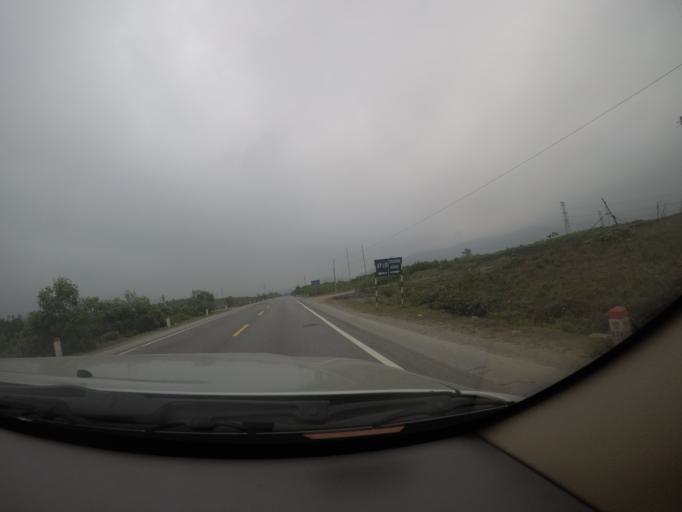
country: VN
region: Ha Tinh
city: Ky Anh
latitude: 18.0352
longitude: 106.3105
